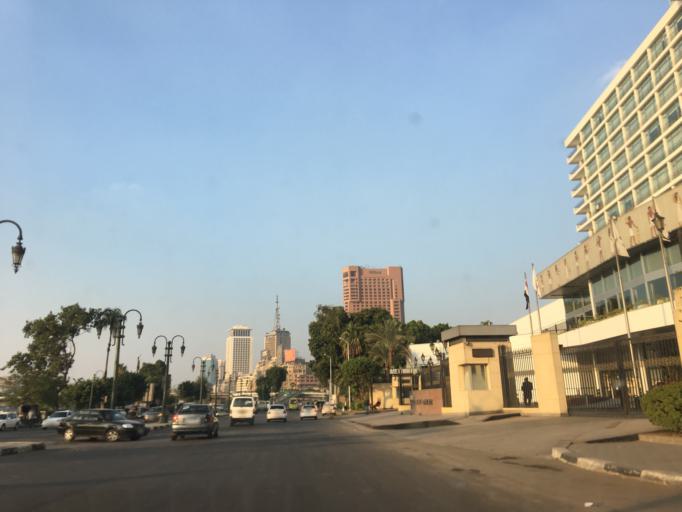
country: EG
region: Muhafazat al Qahirah
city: Cairo
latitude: 30.0456
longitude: 31.2318
